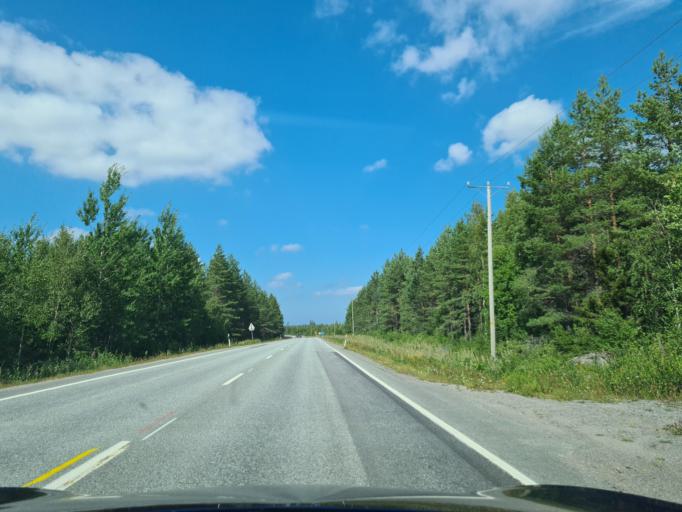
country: FI
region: Ostrobothnia
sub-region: Vaasa
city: Vaasa
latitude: 63.1614
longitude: 21.5917
